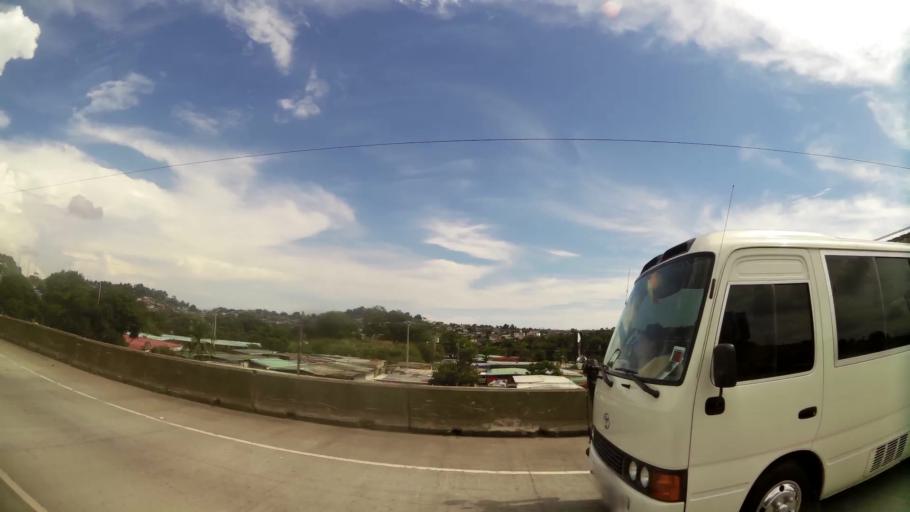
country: PA
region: Panama
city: San Miguelito
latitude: 9.0710
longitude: -79.4944
